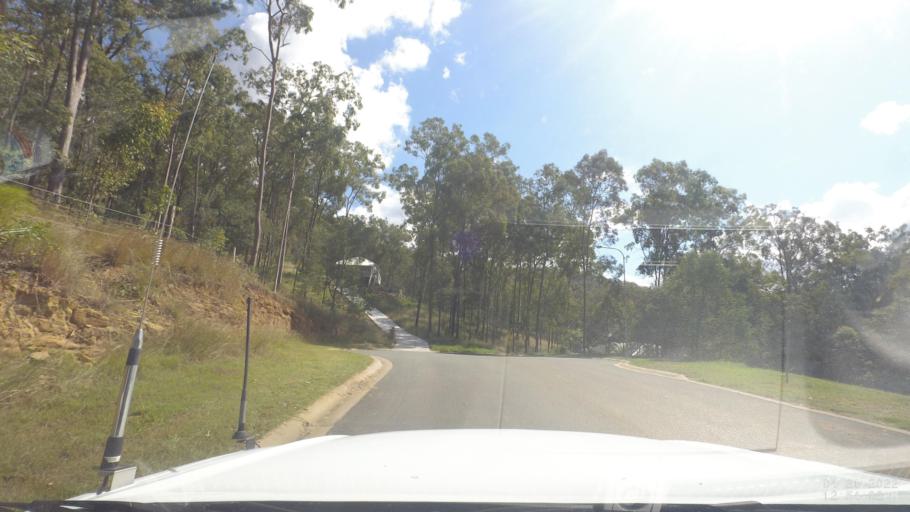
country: AU
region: Queensland
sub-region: Logan
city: Cedar Vale
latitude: -27.8351
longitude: 153.1002
